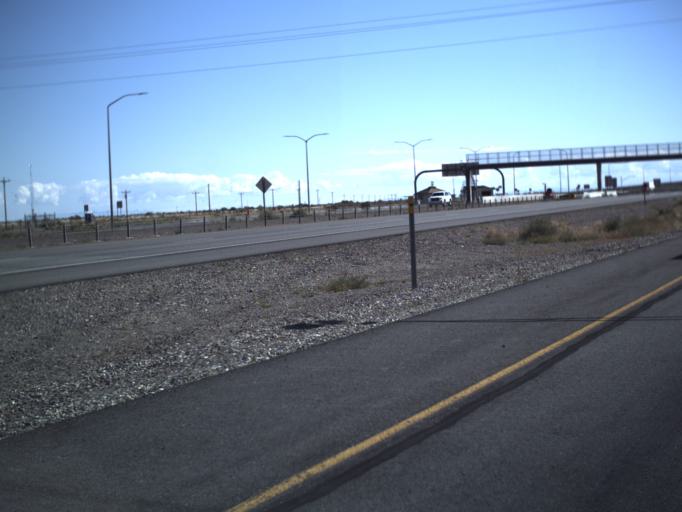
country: US
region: Utah
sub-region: Tooele County
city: Wendover
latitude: 40.7454
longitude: -113.9933
